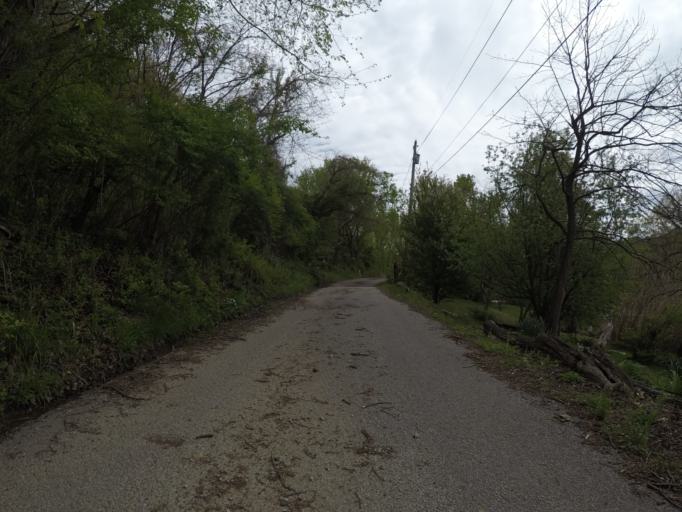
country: US
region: West Virginia
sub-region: Cabell County
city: Huntington
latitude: 38.3960
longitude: -82.4858
